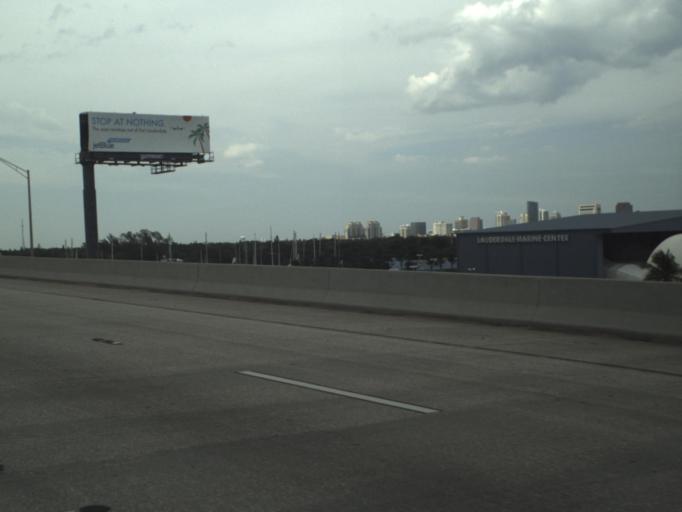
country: US
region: Florida
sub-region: Broward County
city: Boulevard Gardens
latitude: 26.0952
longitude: -80.1686
